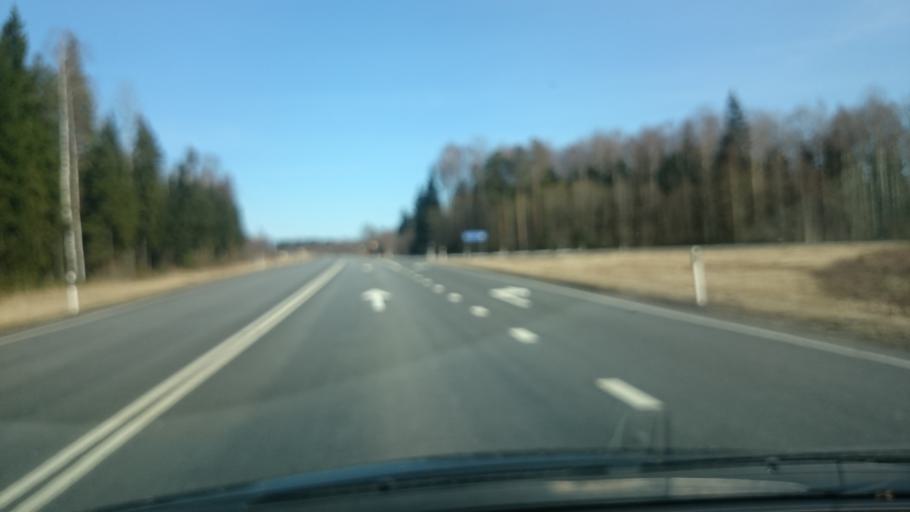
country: EE
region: Paernumaa
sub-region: Vaendra vald (alev)
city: Vandra
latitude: 58.6288
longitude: 24.9453
